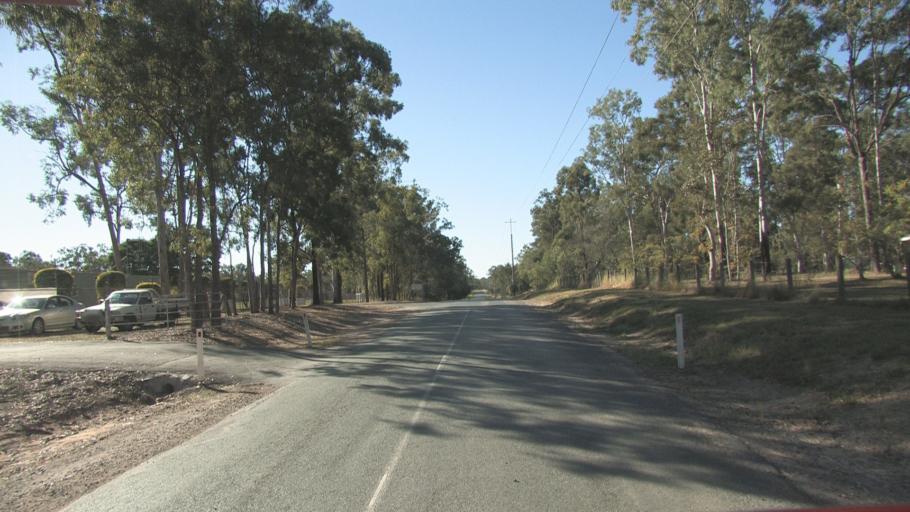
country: AU
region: Queensland
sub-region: Logan
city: North Maclean
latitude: -27.7554
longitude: 153.0133
